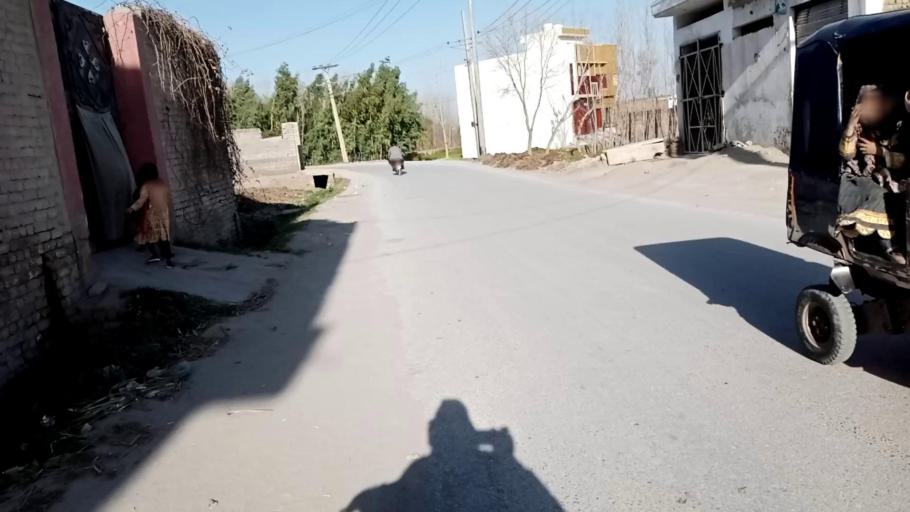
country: PK
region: Khyber Pakhtunkhwa
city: Peshawar
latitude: 34.0495
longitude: 71.5263
